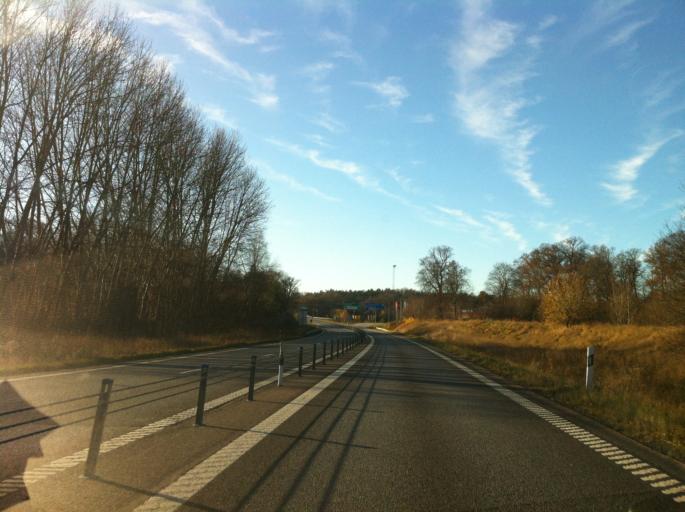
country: SE
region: Blekinge
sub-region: Karlshamns Kommun
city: Karlshamn
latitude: 56.1913
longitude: 14.8692
